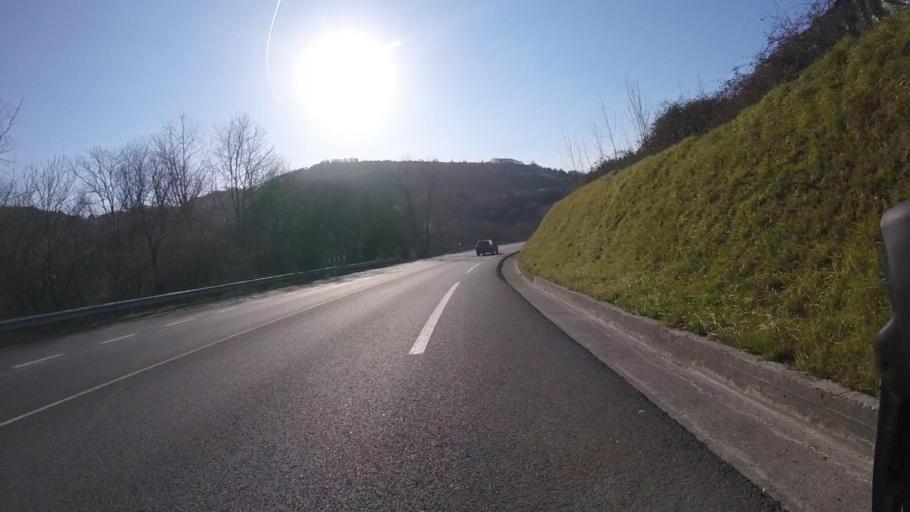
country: ES
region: Basque Country
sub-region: Provincia de Guipuzcoa
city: Astigarraga
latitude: 43.2824
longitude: -1.9231
